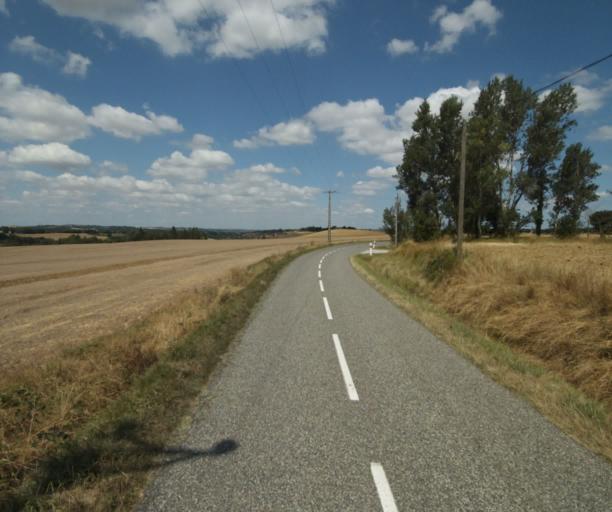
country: FR
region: Midi-Pyrenees
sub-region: Departement de la Haute-Garonne
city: Auriac-sur-Vendinelle
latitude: 43.4717
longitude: 1.8331
